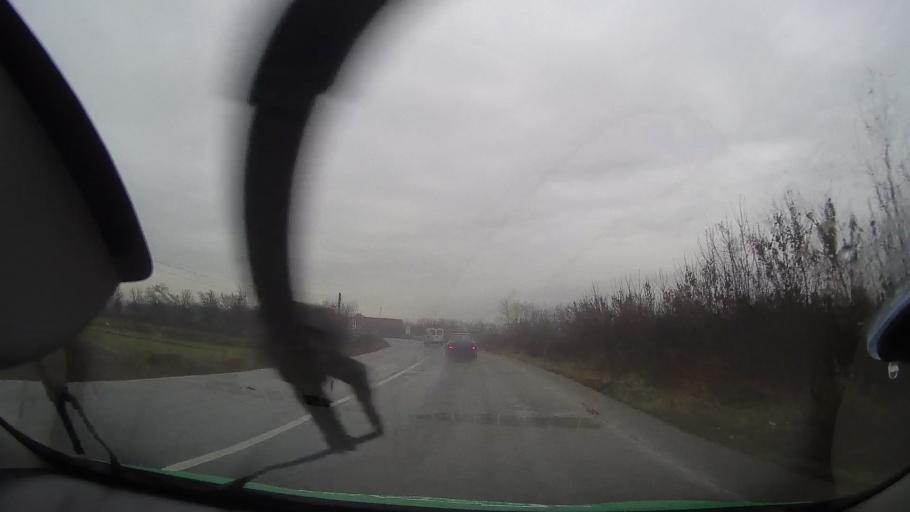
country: RO
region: Bihor
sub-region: Comuna Sambata
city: Sambata
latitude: 46.7948
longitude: 22.2037
